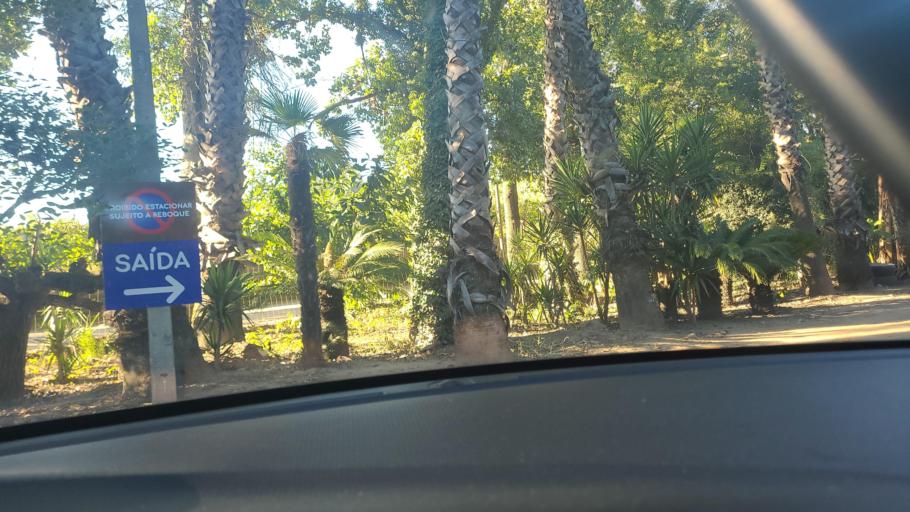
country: PT
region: Braga
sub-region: Amares
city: Amares
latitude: 41.6158
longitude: -8.3487
